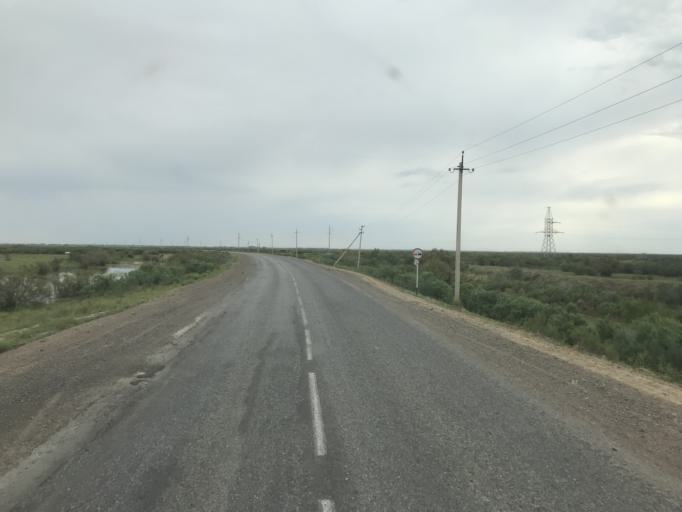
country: KZ
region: Ongtustik Qazaqstan
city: Asykata
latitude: 41.0063
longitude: 68.4750
